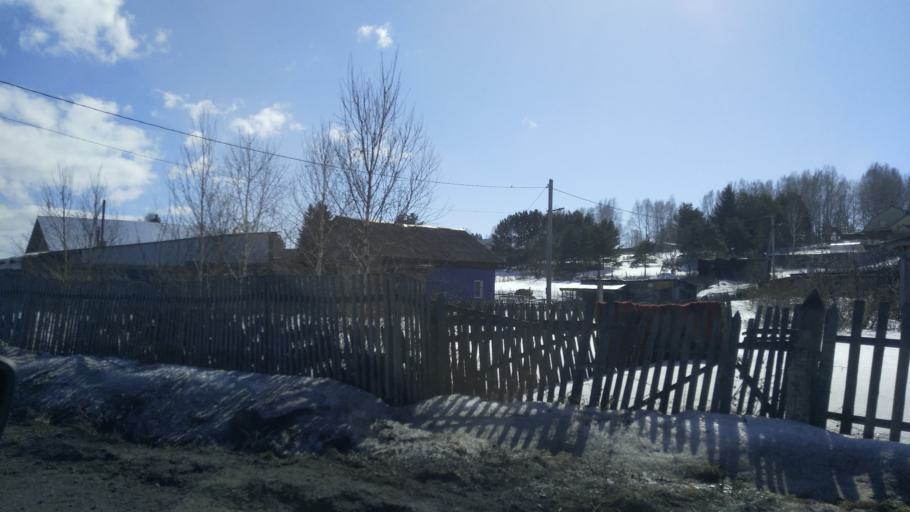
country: RU
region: Kemerovo
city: Yurga
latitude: 55.6988
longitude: 84.9661
